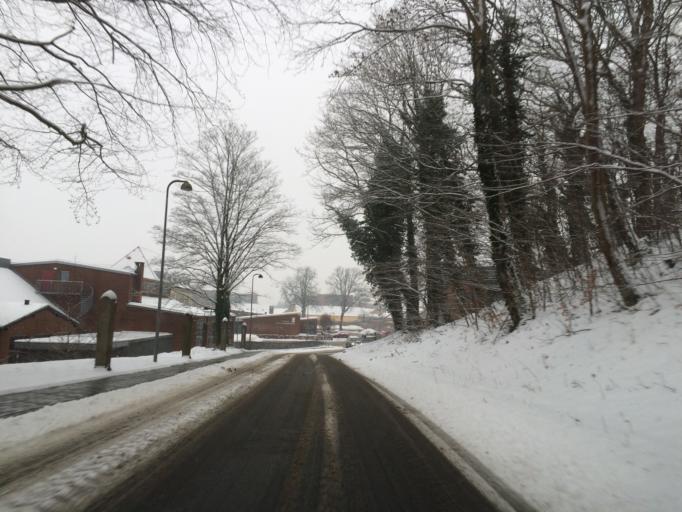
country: DK
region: Central Jutland
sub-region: Silkeborg Kommune
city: Silkeborg
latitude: 56.1710
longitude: 9.5572
